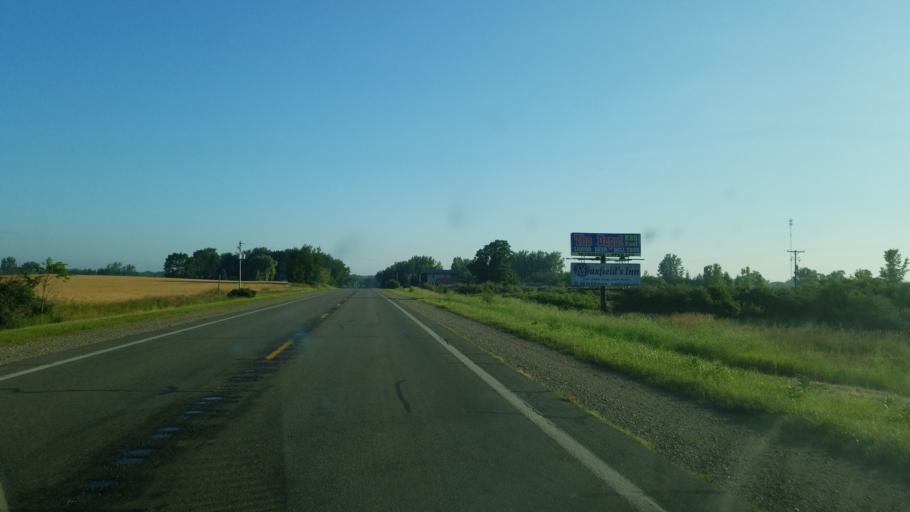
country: US
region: Michigan
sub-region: Montcalm County
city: Edmore
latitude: 43.3992
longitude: -85.0847
